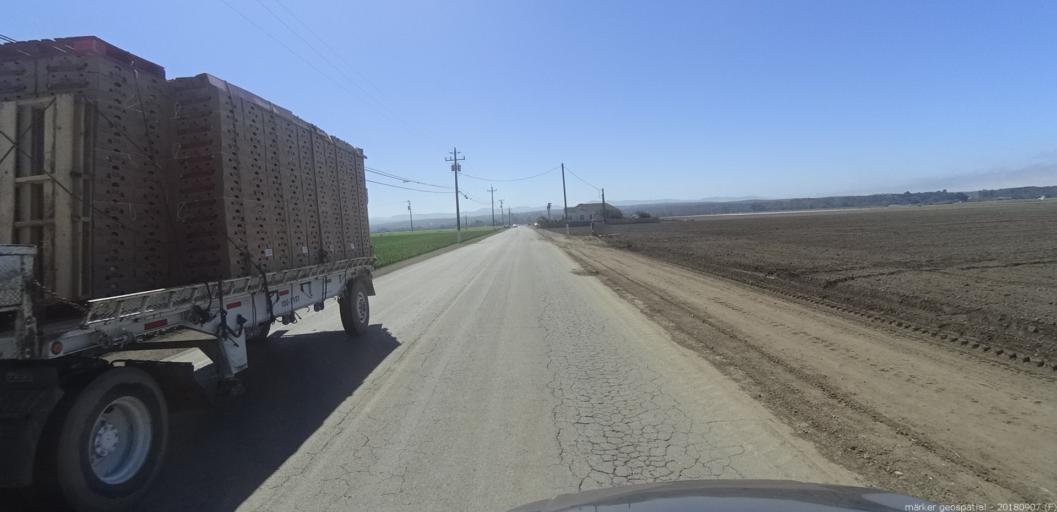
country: US
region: California
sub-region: Monterey County
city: Boronda
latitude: 36.6879
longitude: -121.7350
